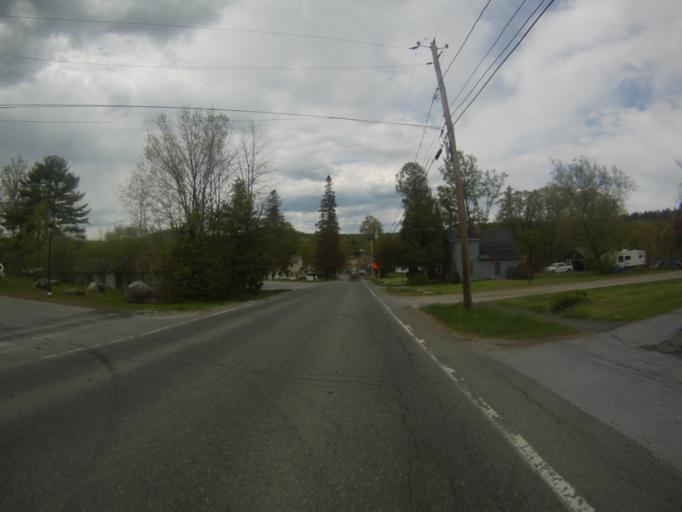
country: US
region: New York
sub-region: Essex County
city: Mineville
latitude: 44.0593
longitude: -73.5093
